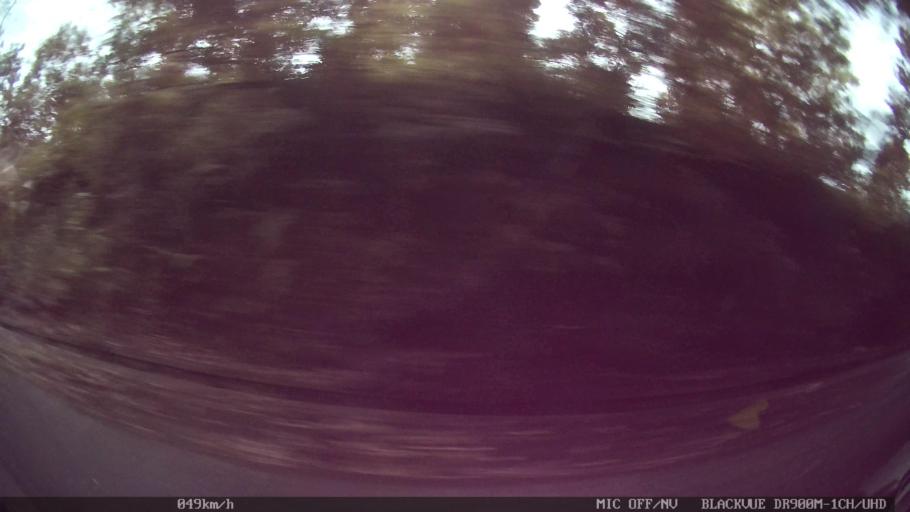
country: ID
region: Bali
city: Banjar Bias
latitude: -8.3745
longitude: 115.4396
